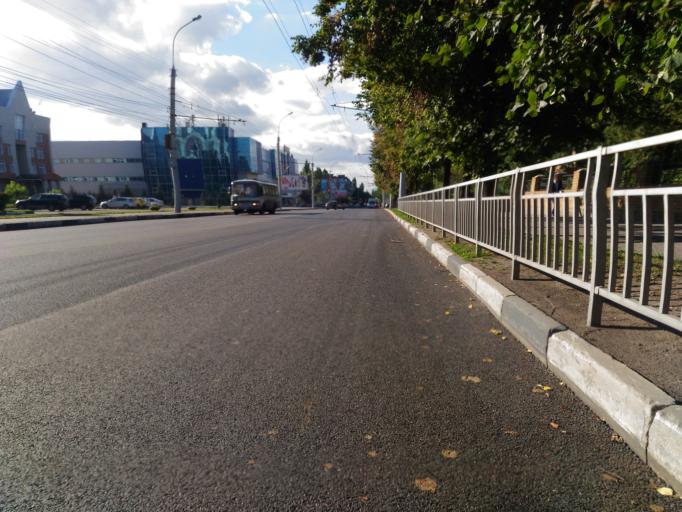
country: RU
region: Voronezj
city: Voronezh
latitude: 51.6517
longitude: 39.1512
